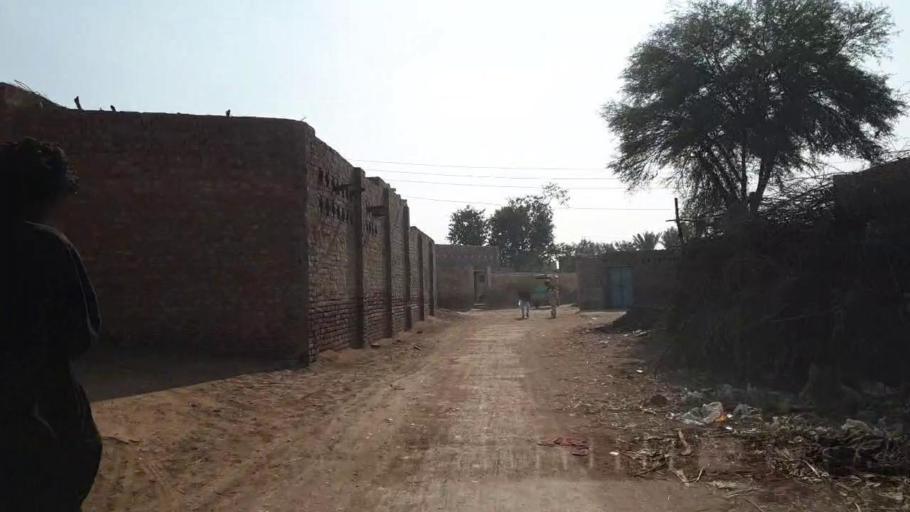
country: PK
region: Sindh
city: Tando Adam
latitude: 25.6837
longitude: 68.5672
